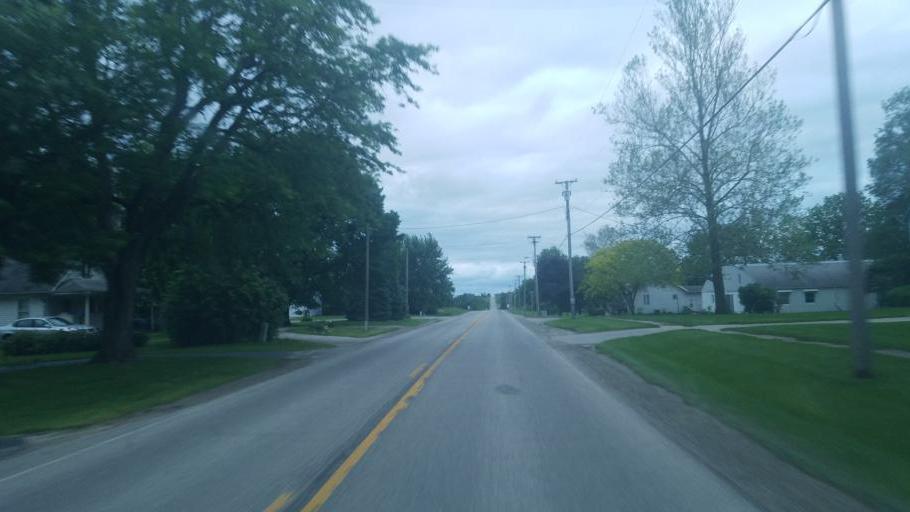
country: US
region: Iowa
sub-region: Decatur County
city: Lamoni
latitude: 40.6154
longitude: -93.9389
